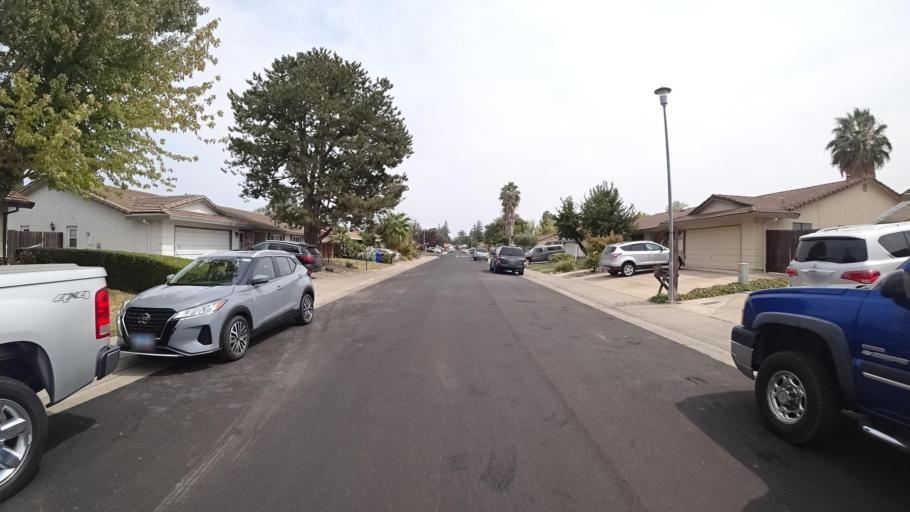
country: US
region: California
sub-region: Sacramento County
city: Elk Grove
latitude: 38.4136
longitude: -121.3843
